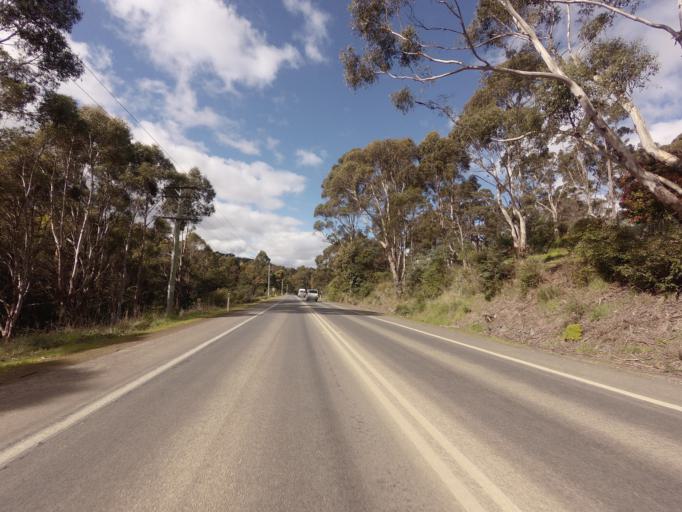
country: AU
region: Tasmania
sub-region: Huon Valley
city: Geeveston
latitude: -43.1652
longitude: 146.9332
